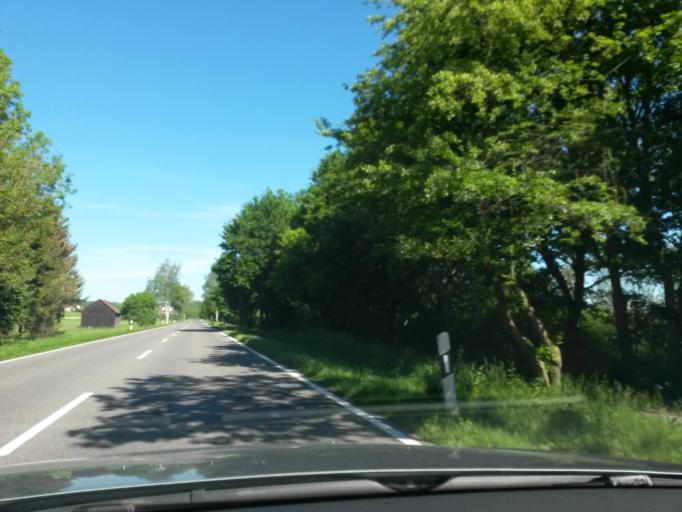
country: DE
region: Baden-Wuerttemberg
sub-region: Tuebingen Region
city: Durnau
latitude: 48.0695
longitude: 9.5692
